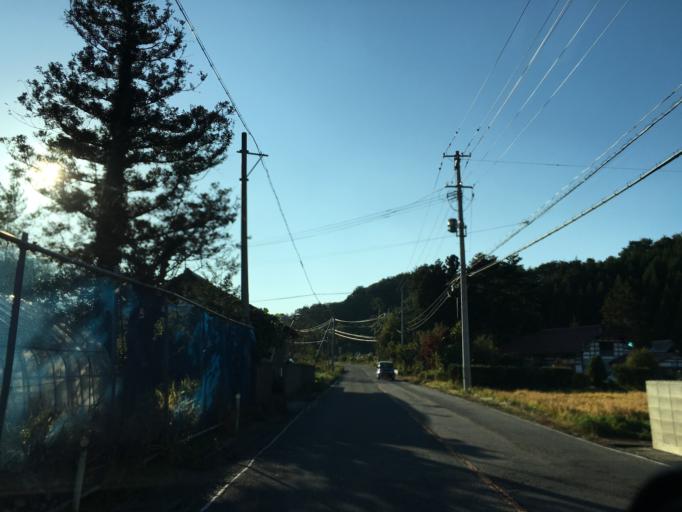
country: JP
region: Fukushima
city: Koriyama
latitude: 37.3981
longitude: 140.2553
